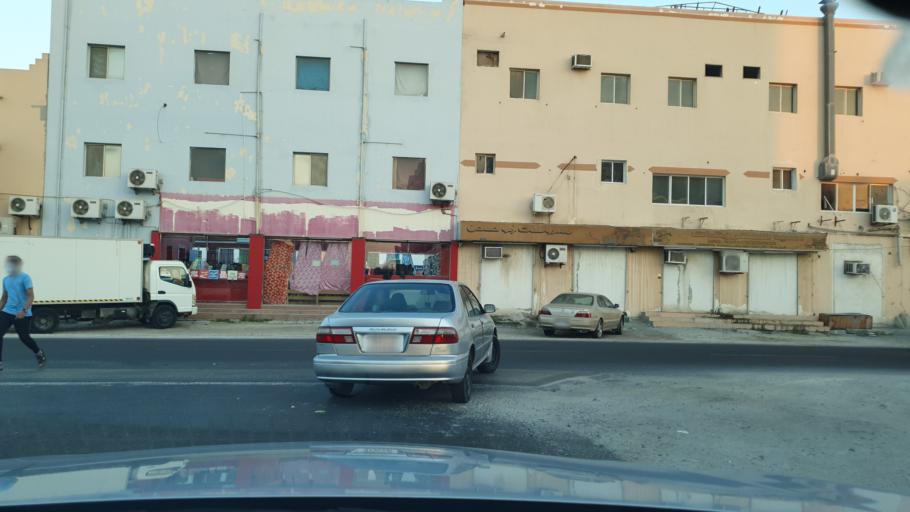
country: BH
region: Northern
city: Madinat `Isa
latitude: 26.1705
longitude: 50.5525
